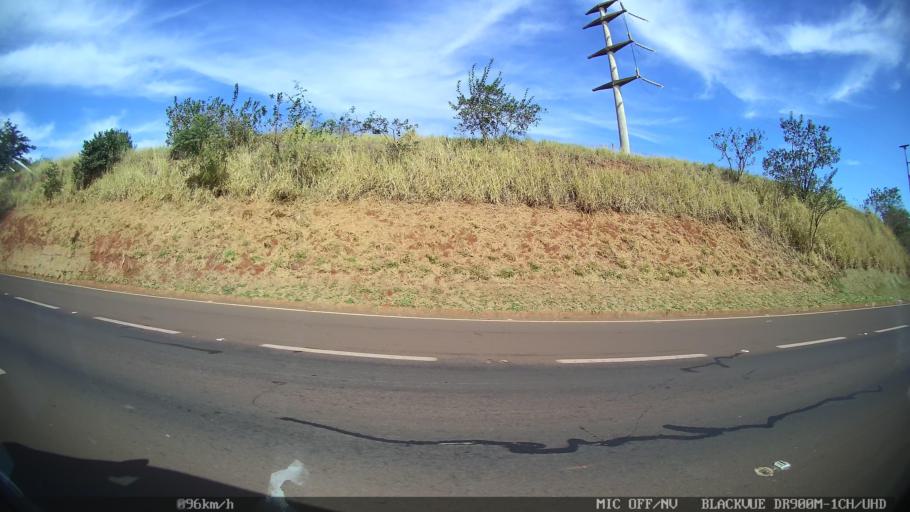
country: BR
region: Sao Paulo
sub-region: Araraquara
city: Araraquara
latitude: -21.8144
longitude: -48.1654
